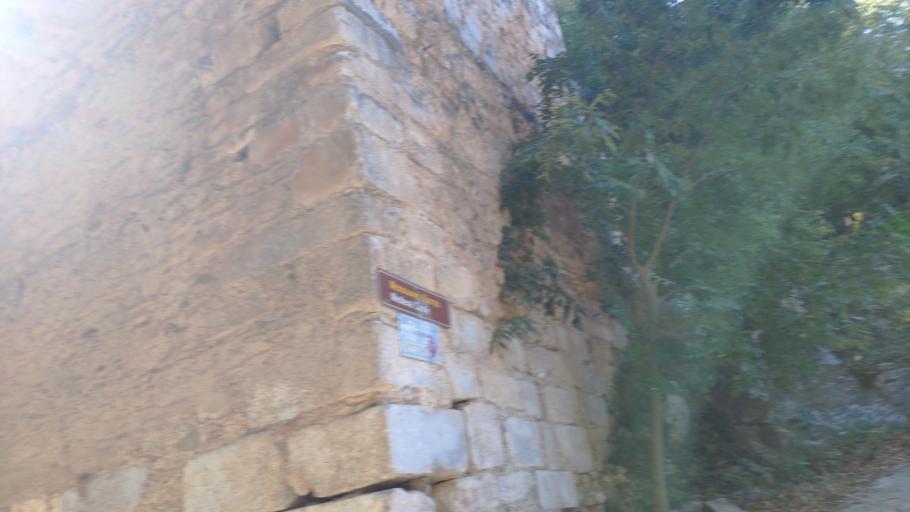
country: GR
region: Central Greece
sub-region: Nomos Voiotias
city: Livadeia
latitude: 38.4317
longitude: 22.8750
